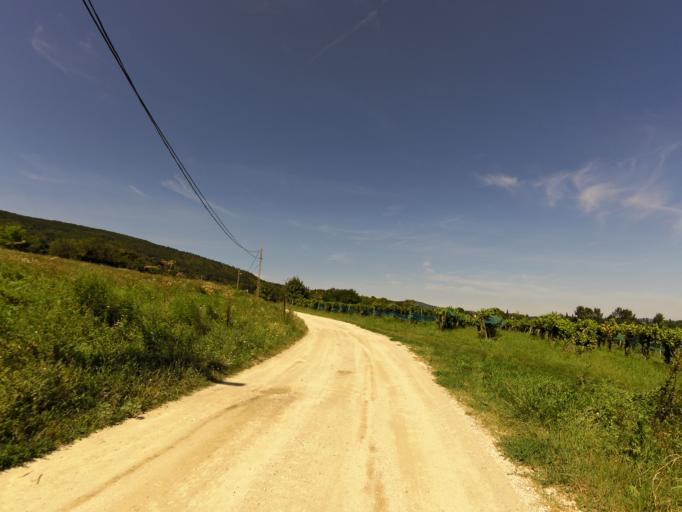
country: HU
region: Zala
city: Vonyarcvashegy
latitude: 46.8164
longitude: 17.3776
